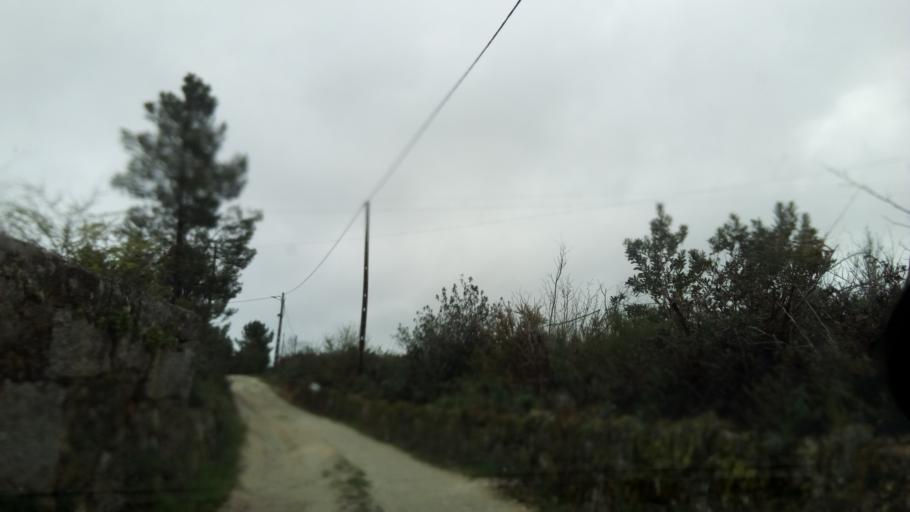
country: PT
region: Guarda
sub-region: Fornos de Algodres
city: Fornos de Algodres
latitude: 40.6200
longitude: -7.5236
